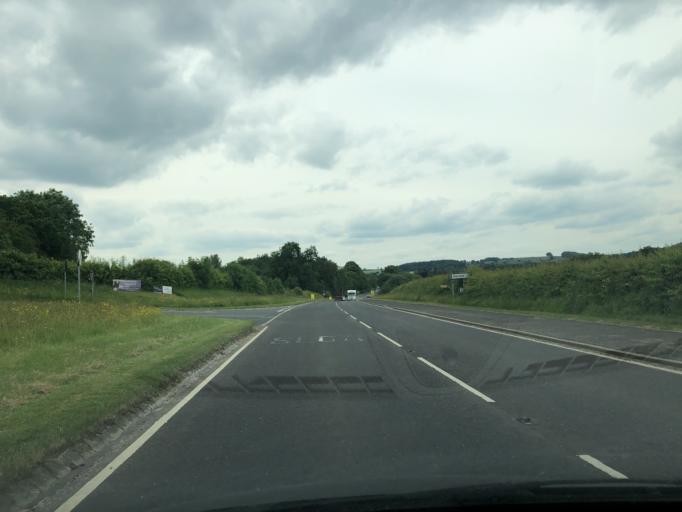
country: GB
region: England
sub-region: North Yorkshire
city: Helmsley
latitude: 54.2470
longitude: -1.0468
